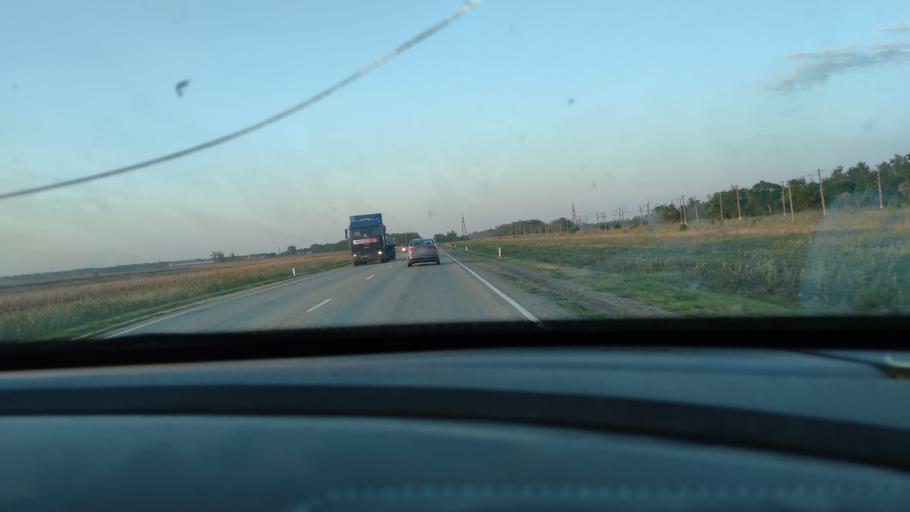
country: RU
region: Krasnodarskiy
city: Starominskaya
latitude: 46.4331
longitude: 39.0173
